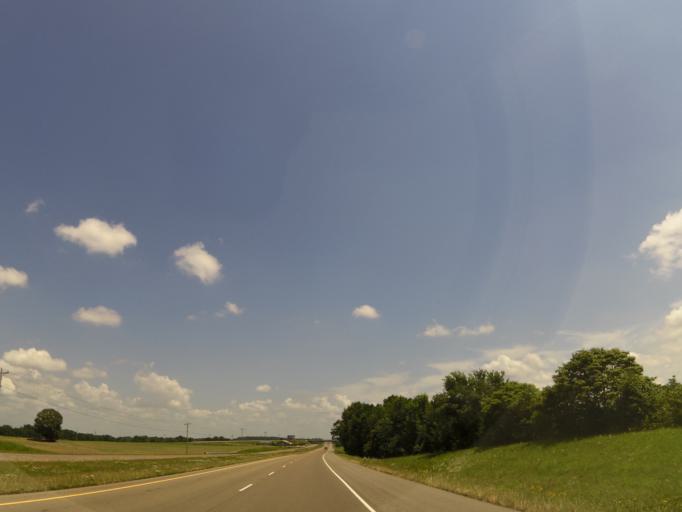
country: US
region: Tennessee
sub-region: Crockett County
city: Alamo
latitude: 35.8904
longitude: -89.2355
